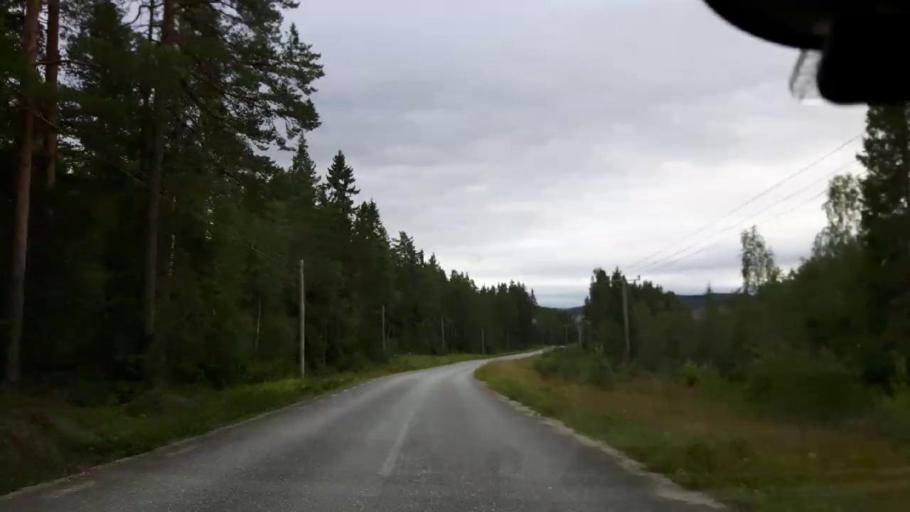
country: SE
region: Jaemtland
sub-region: Braecke Kommun
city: Braecke
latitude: 62.8764
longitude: 15.6174
